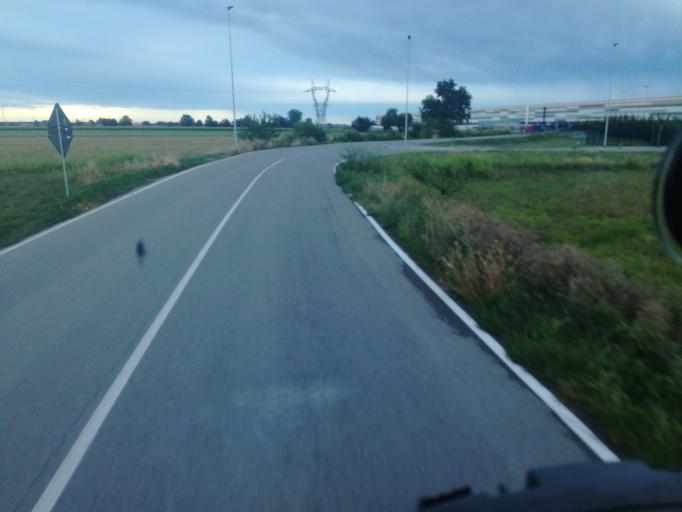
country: IT
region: Emilia-Romagna
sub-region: Provincia di Piacenza
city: Castel San Giovanni
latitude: 45.0807
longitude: 9.4511
